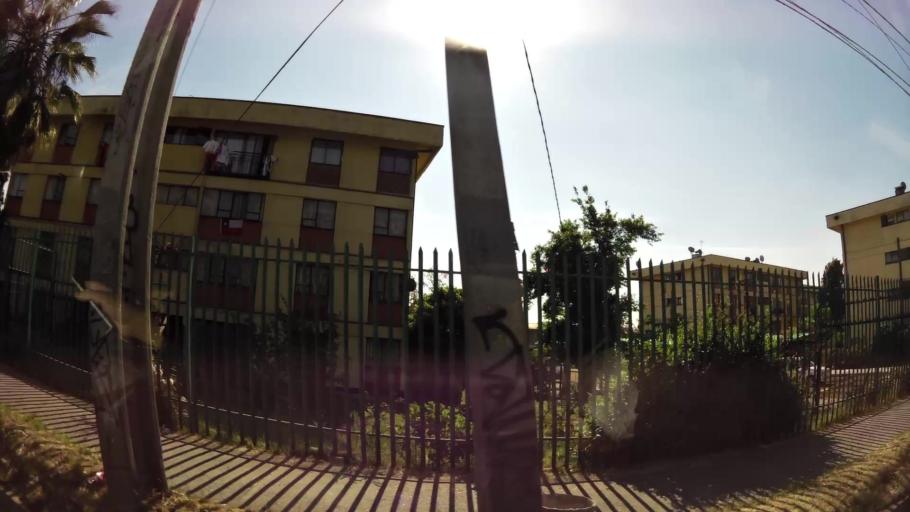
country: CL
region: Santiago Metropolitan
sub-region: Provincia de Santiago
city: Villa Presidente Frei, Nunoa, Santiago, Chile
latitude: -33.4764
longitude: -70.5566
